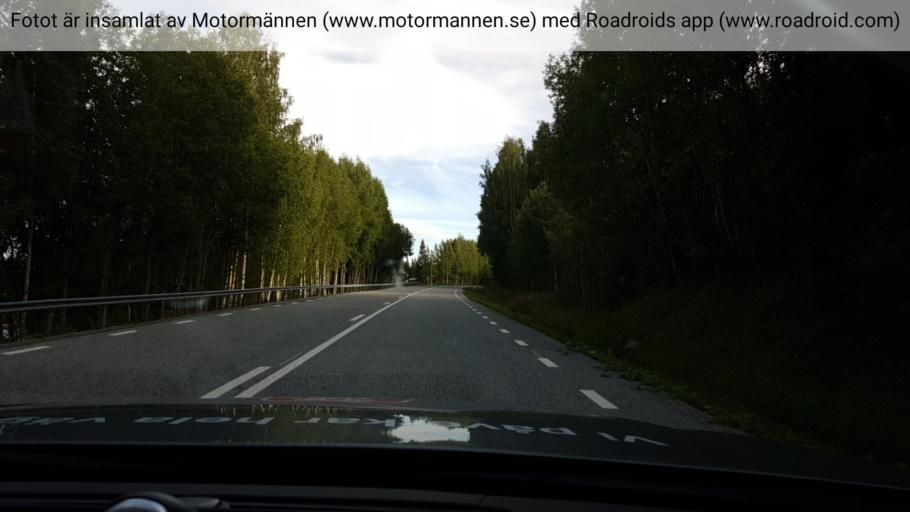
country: SE
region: Jaemtland
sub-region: Stroemsunds Kommun
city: Stroemsund
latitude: 64.1656
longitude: 15.6748
